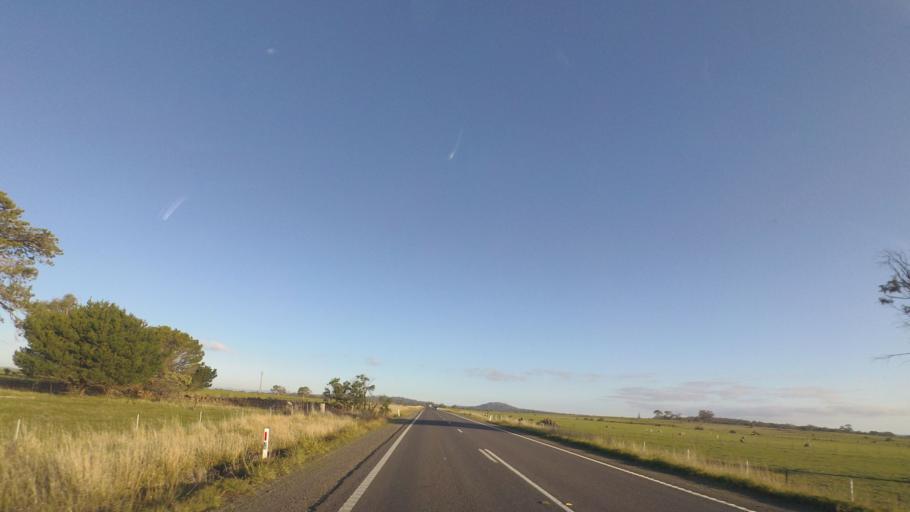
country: AU
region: Victoria
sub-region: Mount Alexander
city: Castlemaine
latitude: -37.1363
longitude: 144.5080
